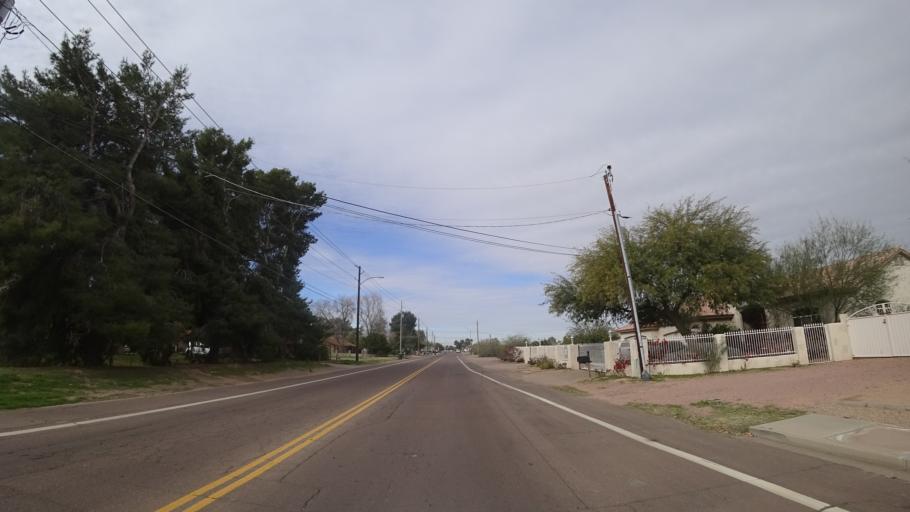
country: US
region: Arizona
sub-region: Maricopa County
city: Peoria
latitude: 33.6619
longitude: -112.1496
